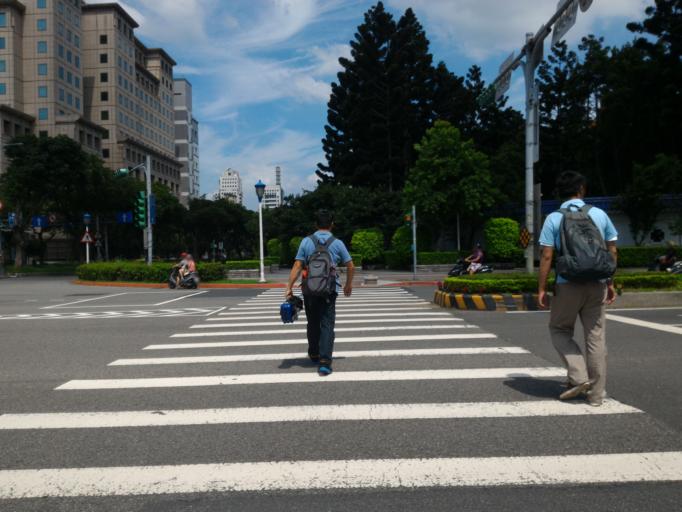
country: TW
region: Taipei
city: Taipei
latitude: 25.0384
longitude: 121.5174
